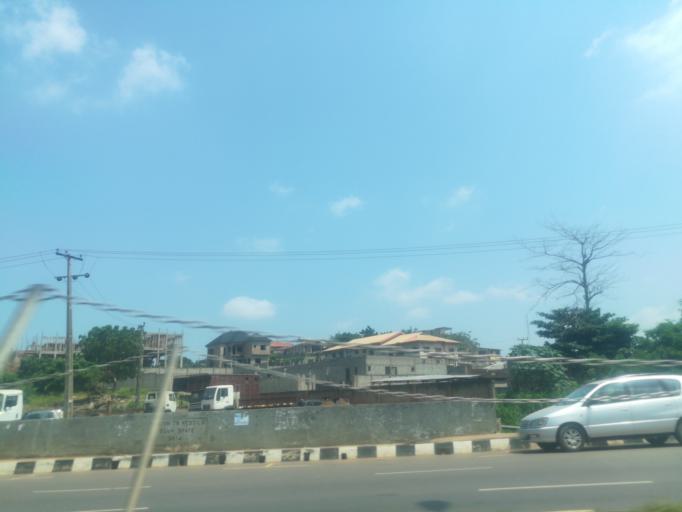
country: NG
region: Ogun
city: Abeokuta
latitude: 7.1407
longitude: 3.3644
